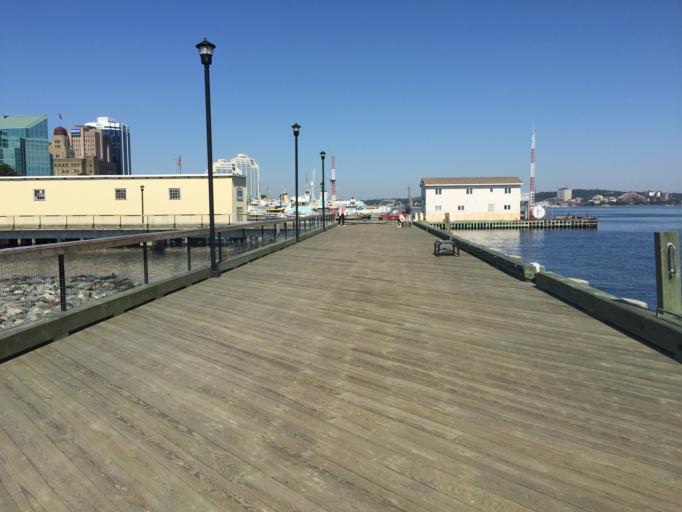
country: CA
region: Nova Scotia
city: Halifax
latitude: 44.6454
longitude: -63.5680
